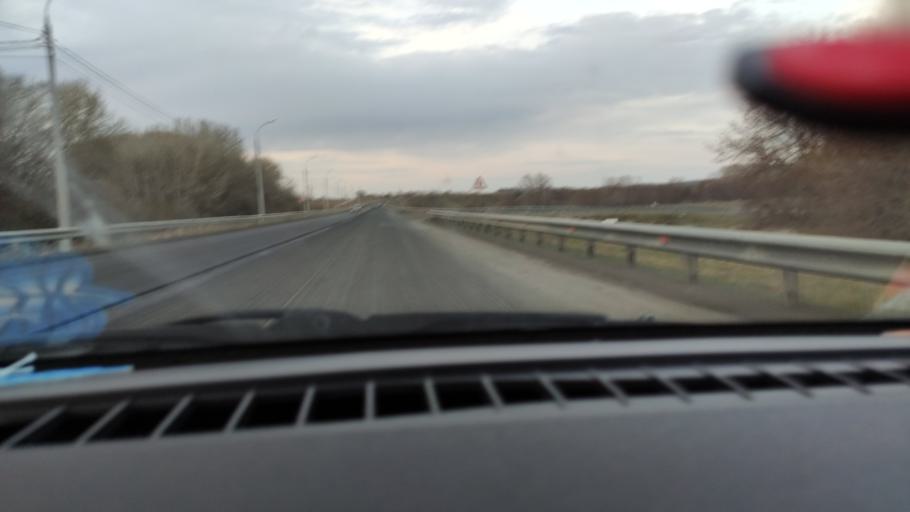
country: RU
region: Saratov
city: Yelshanka
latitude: 51.8268
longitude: 46.2228
